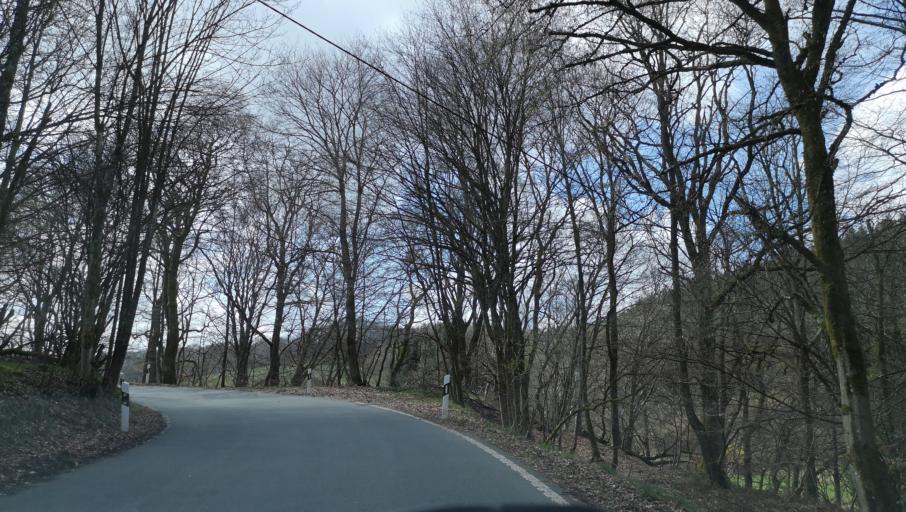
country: DE
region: North Rhine-Westphalia
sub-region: Regierungsbezirk Arnsberg
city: Breckerfeld
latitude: 51.2505
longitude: 7.4143
